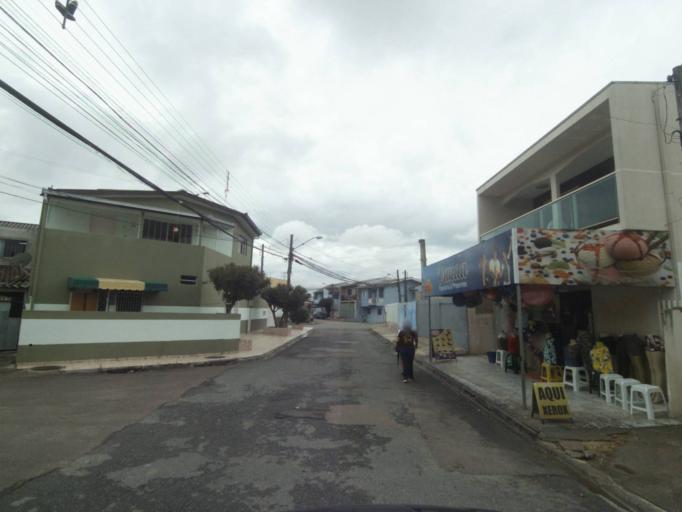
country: BR
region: Parana
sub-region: Curitiba
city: Curitiba
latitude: -25.4708
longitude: -49.3245
